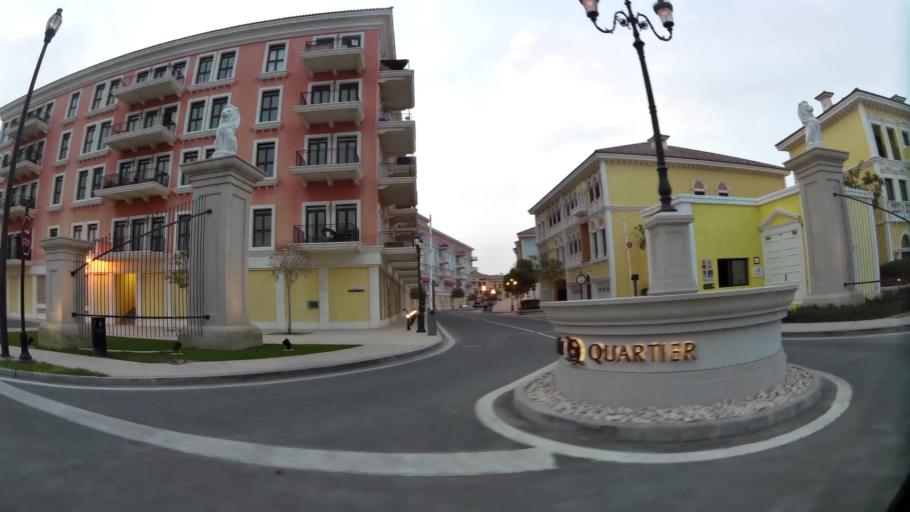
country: QA
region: Baladiyat ad Dawhah
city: Doha
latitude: 25.3788
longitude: 51.5470
